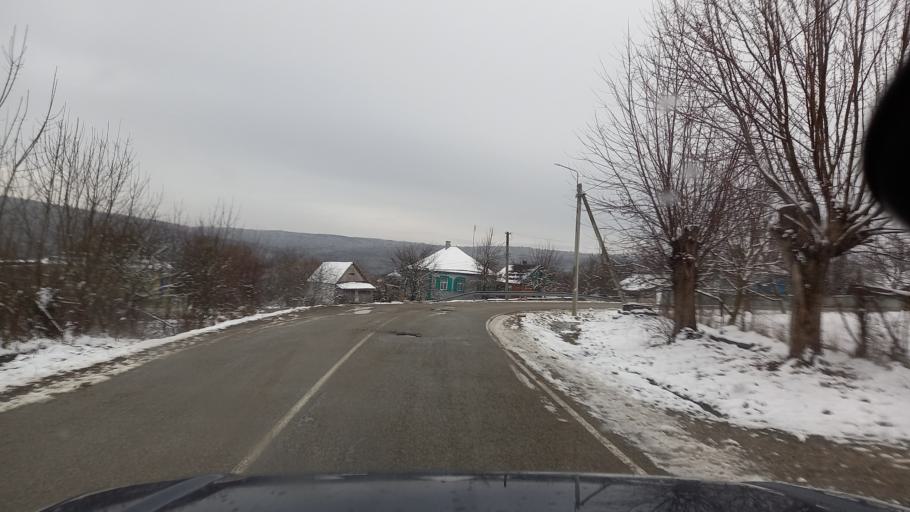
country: RU
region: Adygeya
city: Abadzekhskaya
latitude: 44.3572
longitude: 40.4082
